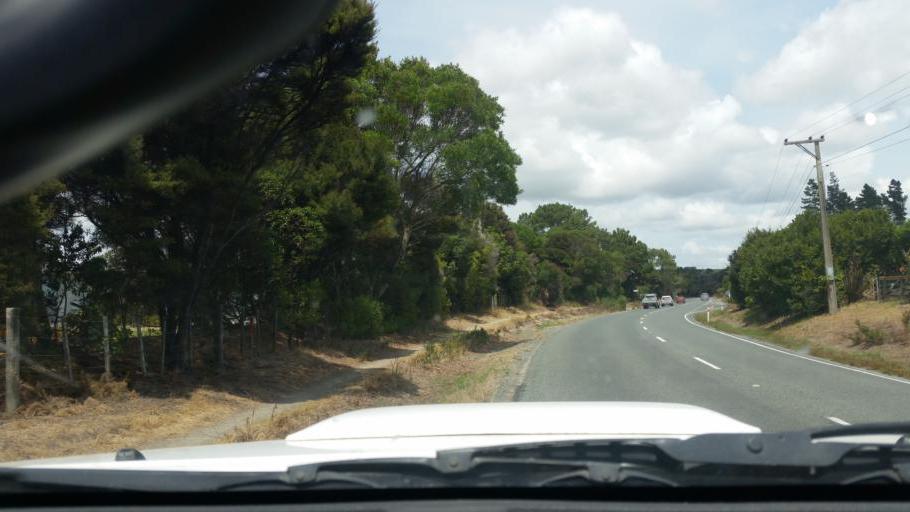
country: NZ
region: Auckland
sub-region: Auckland
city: Wellsford
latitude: -36.1157
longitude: 174.5749
